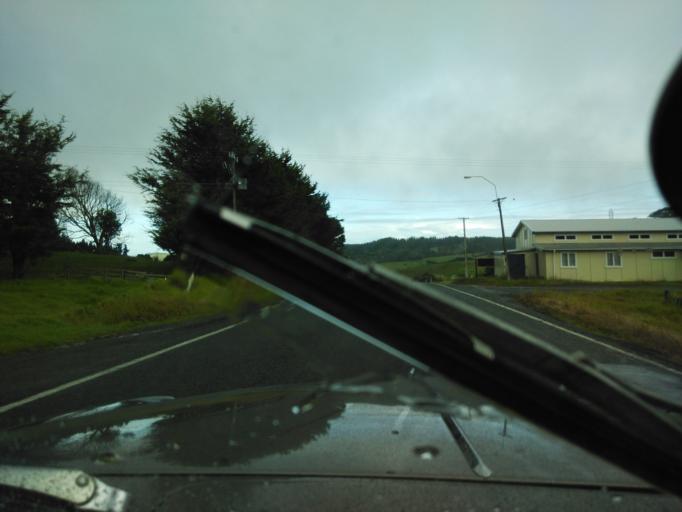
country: NZ
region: Auckland
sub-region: Auckland
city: Parakai
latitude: -36.4740
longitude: 174.4490
